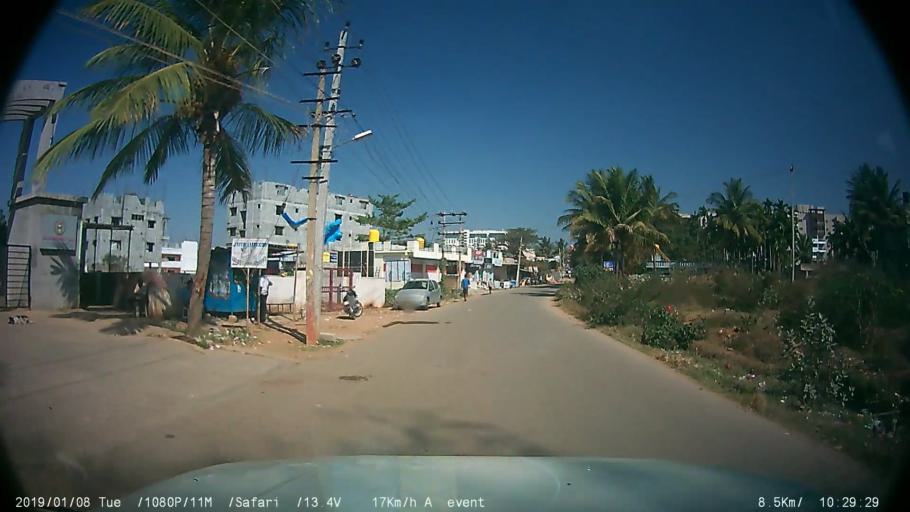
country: IN
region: Karnataka
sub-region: Bangalore Urban
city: Anekal
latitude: 12.8302
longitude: 77.6551
